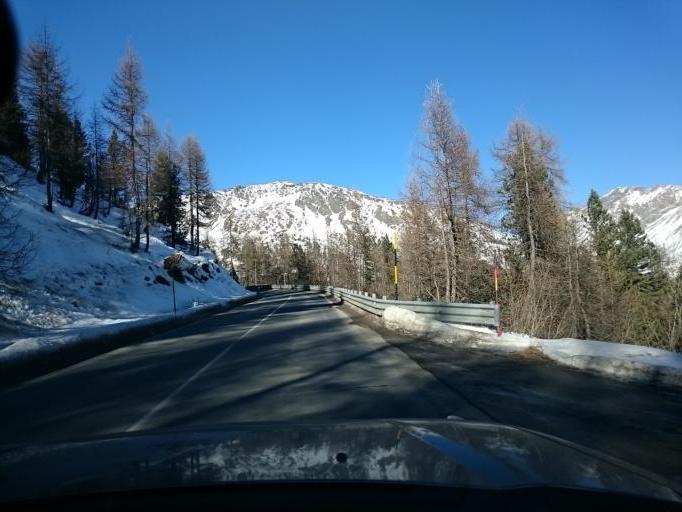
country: IT
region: Lombardy
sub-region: Provincia di Sondrio
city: Isolaccia
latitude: 46.4787
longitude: 10.2474
